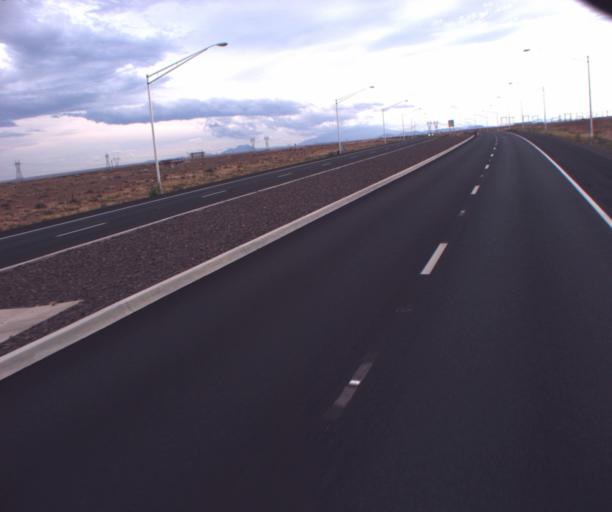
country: US
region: Arizona
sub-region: Coconino County
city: Tuba City
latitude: 35.8478
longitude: -111.4314
